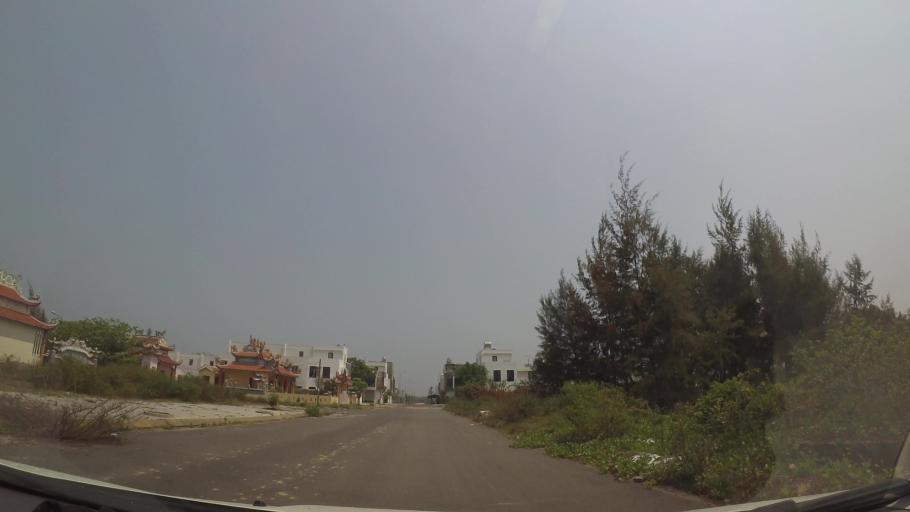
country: VN
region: Da Nang
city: Ngu Hanh Son
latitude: 15.9758
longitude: 108.2601
